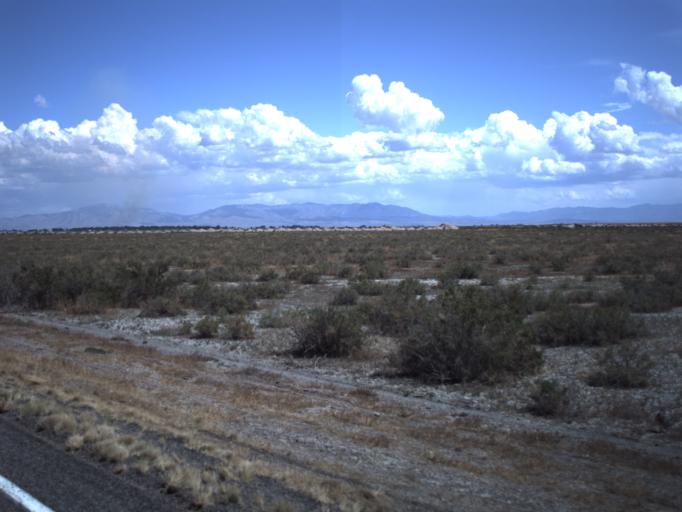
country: US
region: Utah
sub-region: Millard County
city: Delta
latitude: 39.3175
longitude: -112.7466
